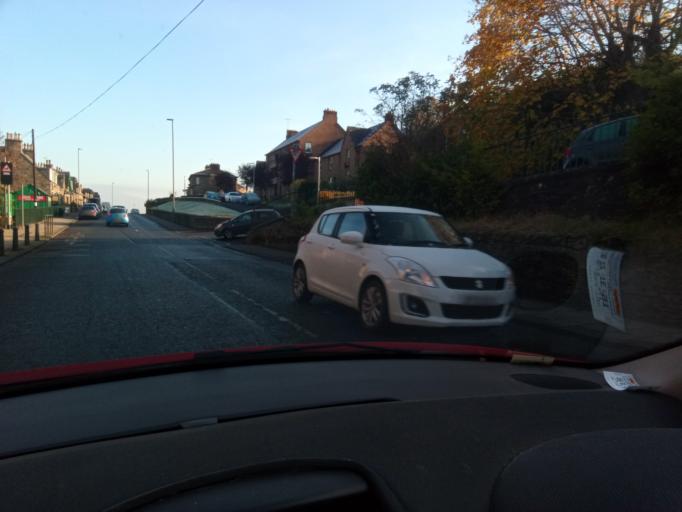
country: GB
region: Scotland
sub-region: The Scottish Borders
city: Hawick
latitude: 55.4272
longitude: -2.7785
